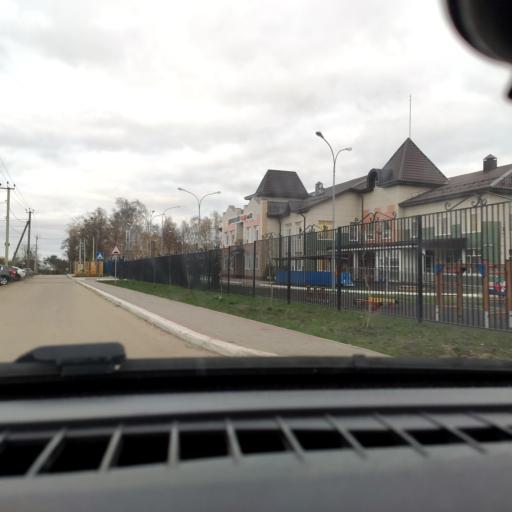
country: RU
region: Voronezj
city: Podgornoye
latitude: 51.7294
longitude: 39.1621
